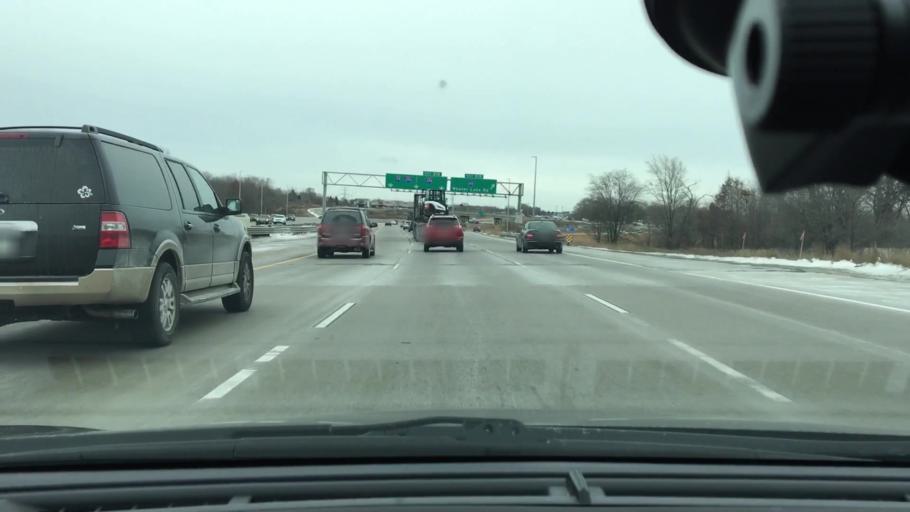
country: US
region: Minnesota
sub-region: Hennepin County
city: Maple Grove
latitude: 45.1080
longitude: -93.4667
